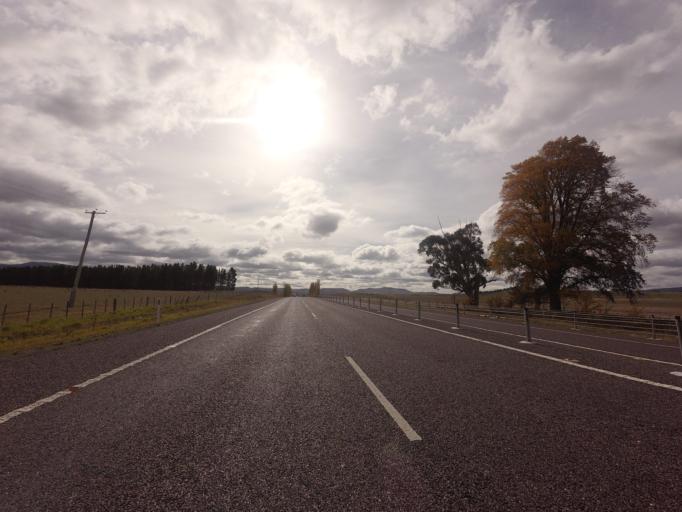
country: AU
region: Tasmania
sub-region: Brighton
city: Bridgewater
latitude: -42.5097
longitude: 147.1887
